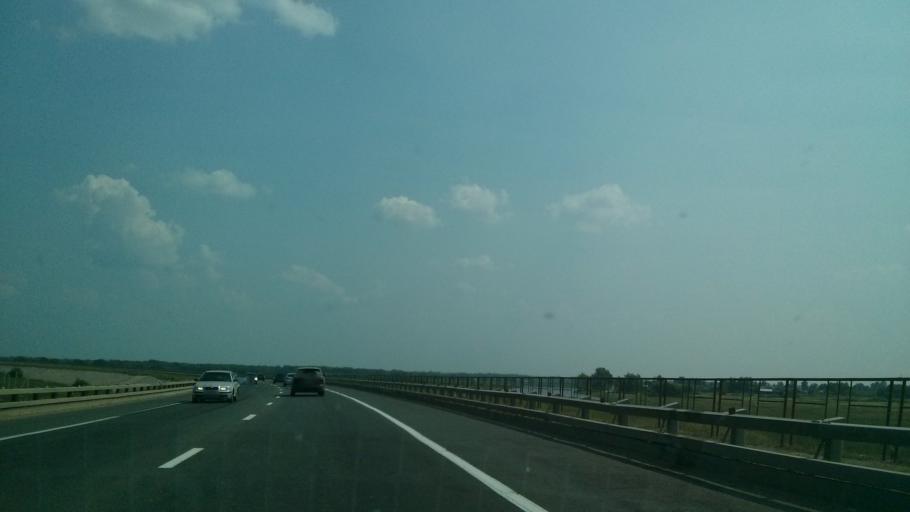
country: RU
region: Vladimir
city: Murom
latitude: 55.5907
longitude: 42.1185
